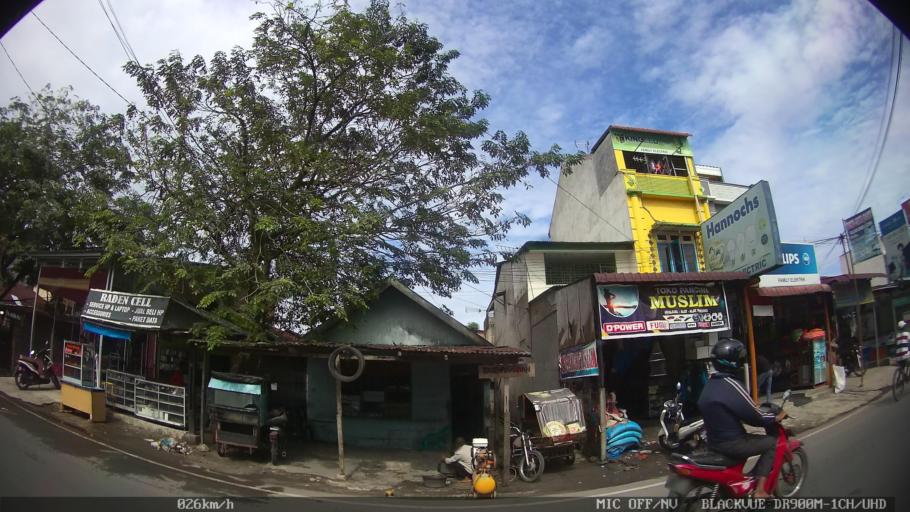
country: ID
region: North Sumatra
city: Sunggal
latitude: 3.6087
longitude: 98.6081
